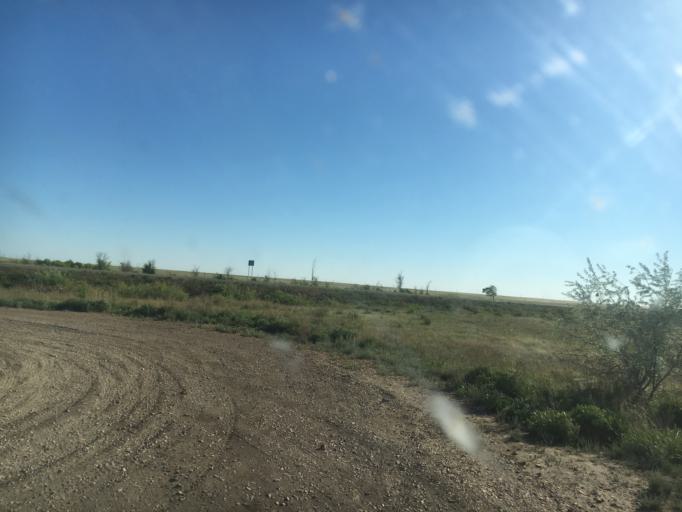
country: RU
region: Orenburg
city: Dombarovskiy
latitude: 50.1076
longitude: 59.3441
